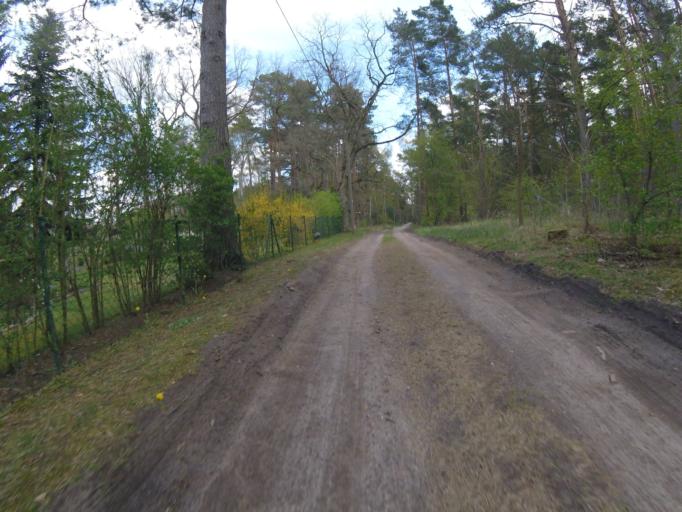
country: DE
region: Brandenburg
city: Gross Koris
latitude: 52.2169
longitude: 13.7619
